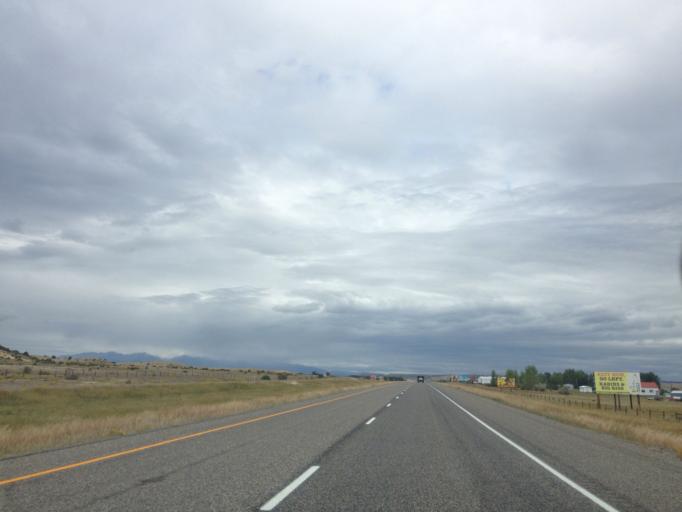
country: US
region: Montana
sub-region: Sweet Grass County
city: Big Timber
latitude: 45.7589
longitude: -109.7843
